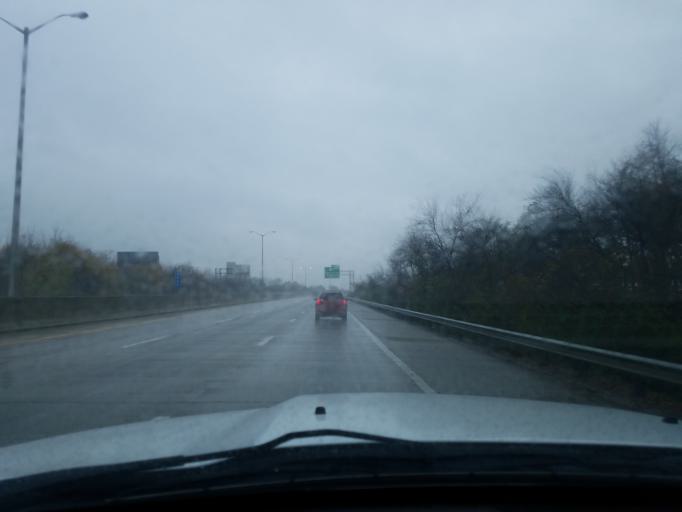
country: US
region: Kentucky
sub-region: Jefferson County
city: Shively
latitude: 38.2170
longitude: -85.8226
